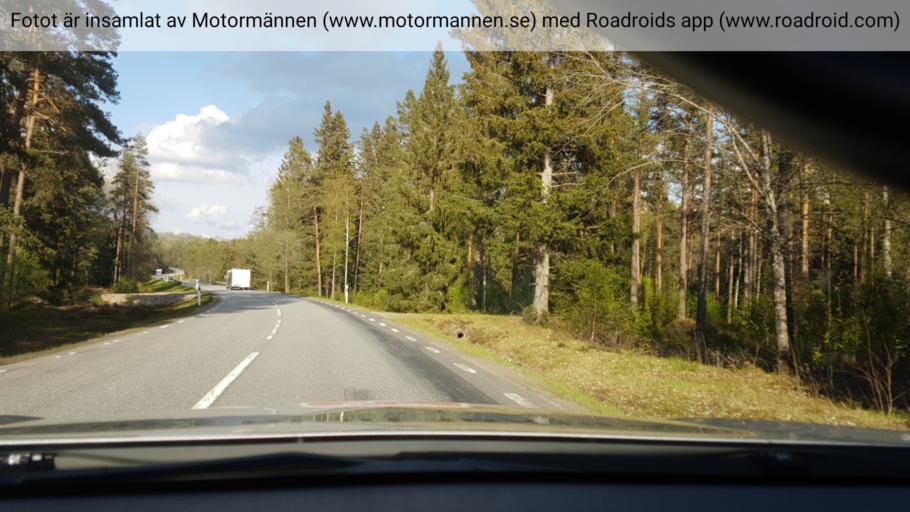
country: SE
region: Joenkoeping
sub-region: Vaggeryds Kommun
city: Skillingaryd
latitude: 57.3862
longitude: 14.0034
